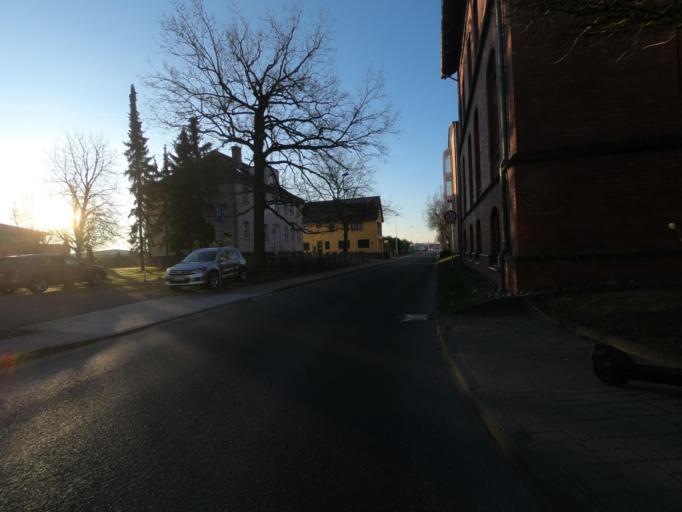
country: DE
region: Mecklenburg-Vorpommern
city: Rostock
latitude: 54.0761
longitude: 12.1419
